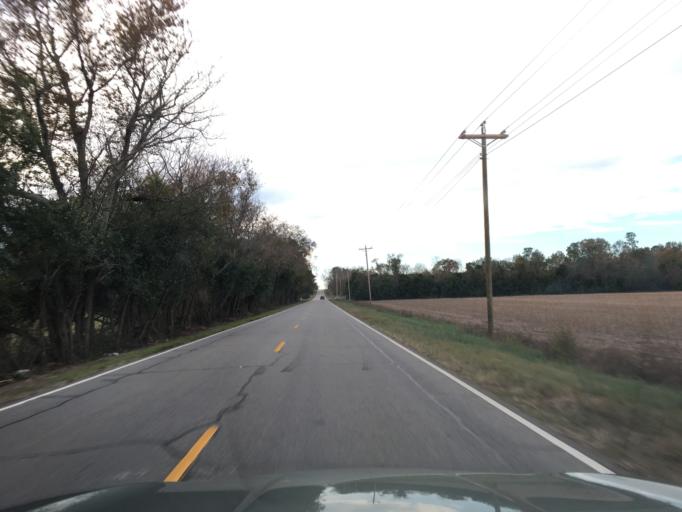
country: US
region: South Carolina
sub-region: Lexington County
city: Leesville
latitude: 33.7666
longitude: -81.3835
